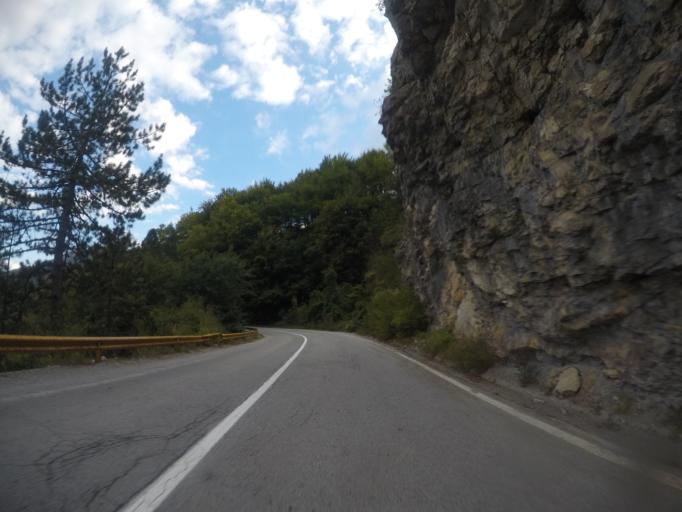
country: ME
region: Mojkovac
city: Mojkovac
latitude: 43.0053
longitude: 19.4341
